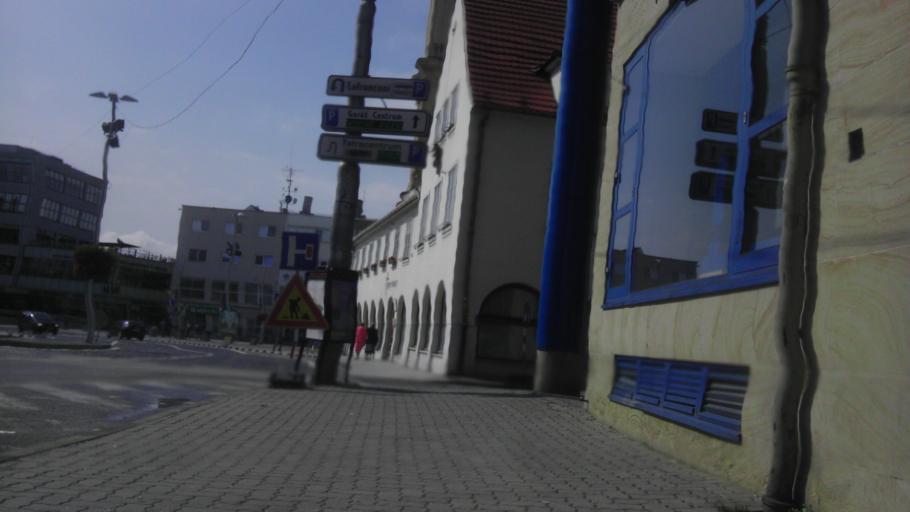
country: SK
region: Bratislavsky
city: Bratislava
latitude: 48.1466
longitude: 17.1069
